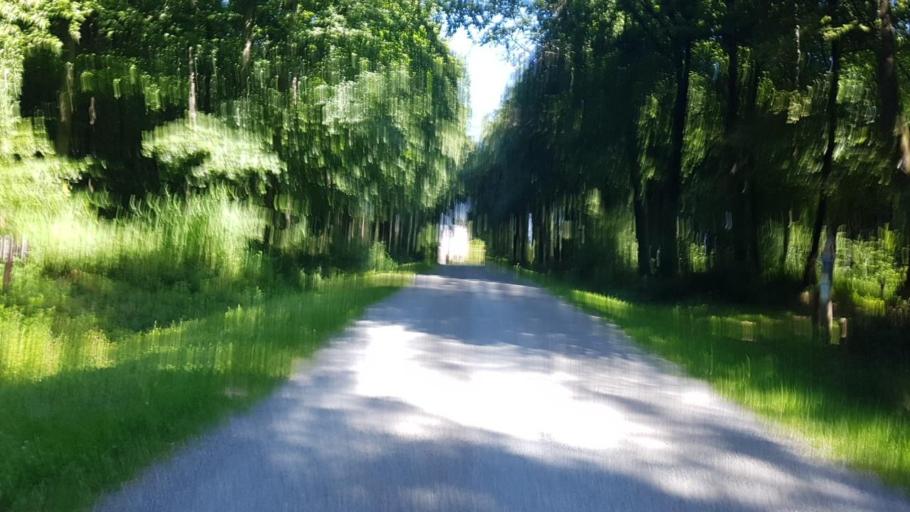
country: BE
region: Wallonia
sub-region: Province du Hainaut
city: Momignies
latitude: 50.0369
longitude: 4.2001
